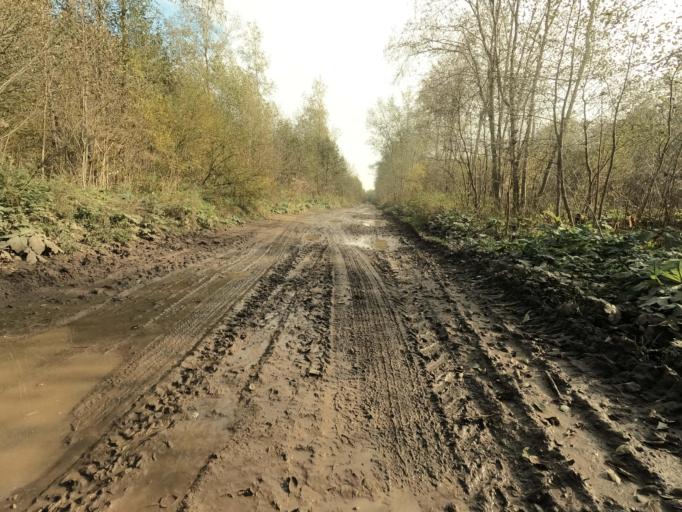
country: RU
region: Novgorod
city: Batetskiy
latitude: 58.8796
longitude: 30.7380
